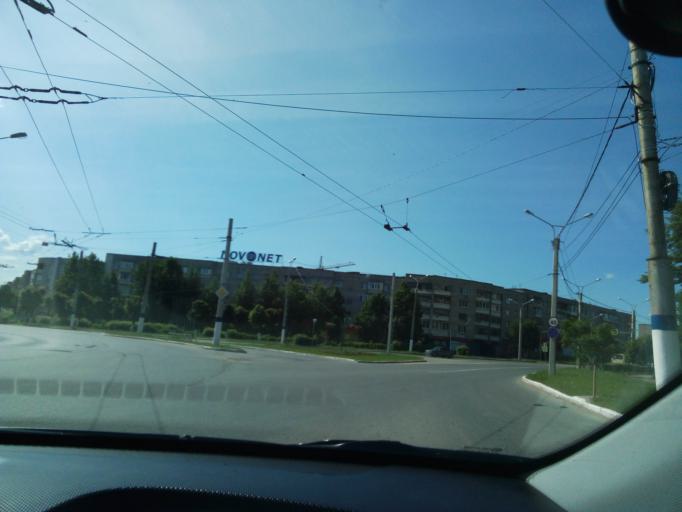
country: RU
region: Chuvashia
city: Novocheboksarsk
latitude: 56.1141
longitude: 47.4862
